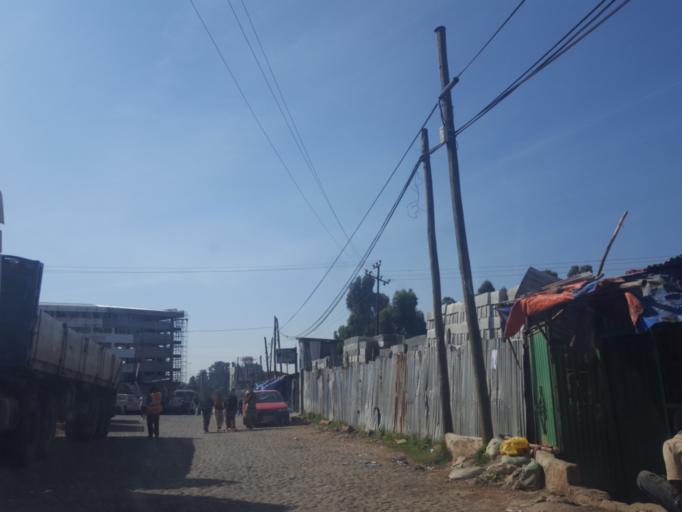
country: ET
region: Adis Abeba
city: Addis Ababa
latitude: 9.0596
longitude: 38.7132
